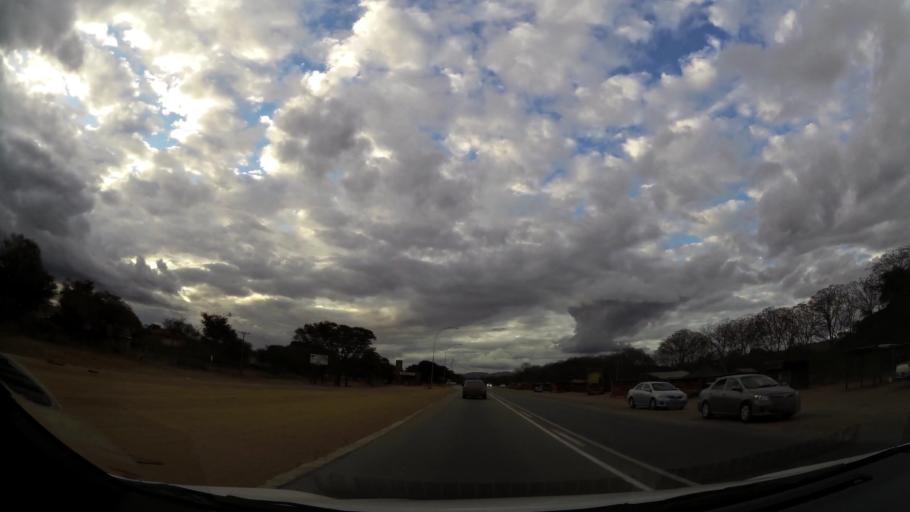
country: ZA
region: Limpopo
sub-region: Waterberg District Municipality
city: Mokopane
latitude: -24.2127
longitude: 29.0058
